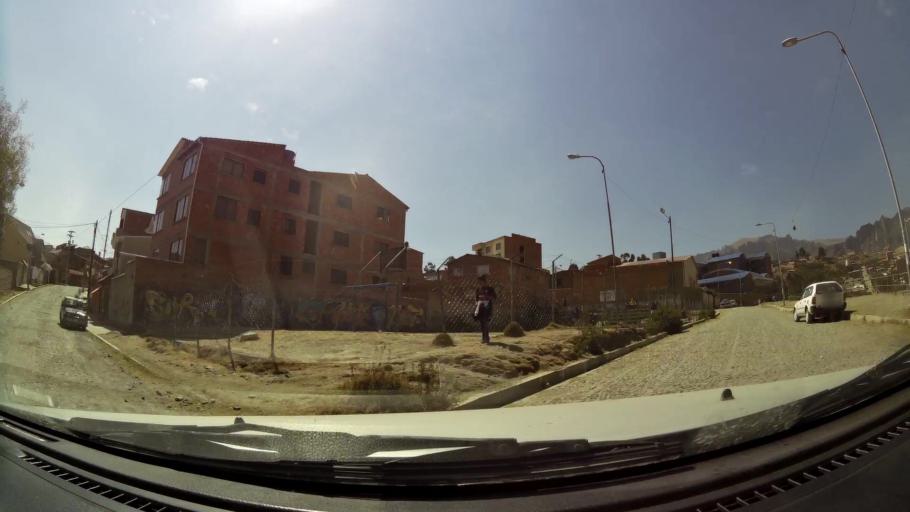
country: BO
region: La Paz
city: La Paz
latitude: -16.5390
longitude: -68.0460
